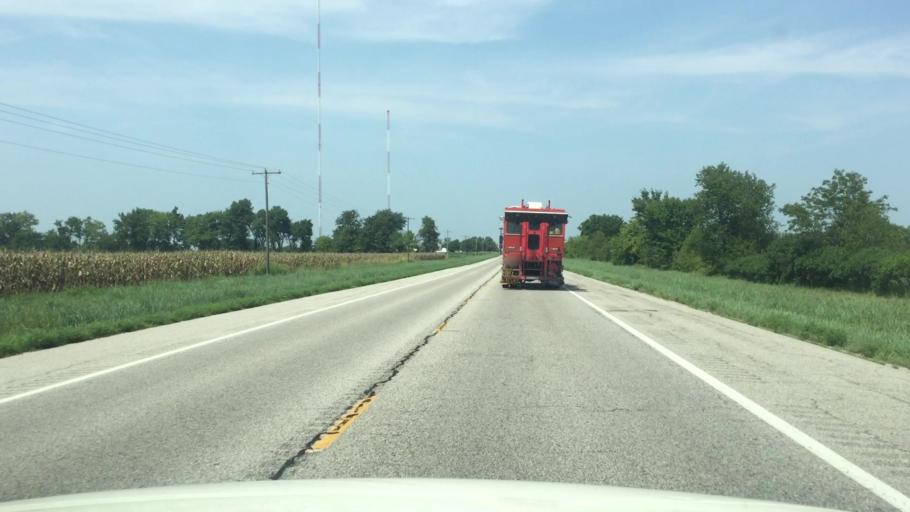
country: US
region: Missouri
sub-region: Jasper County
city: Carl Junction
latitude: 37.2121
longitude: -94.7048
